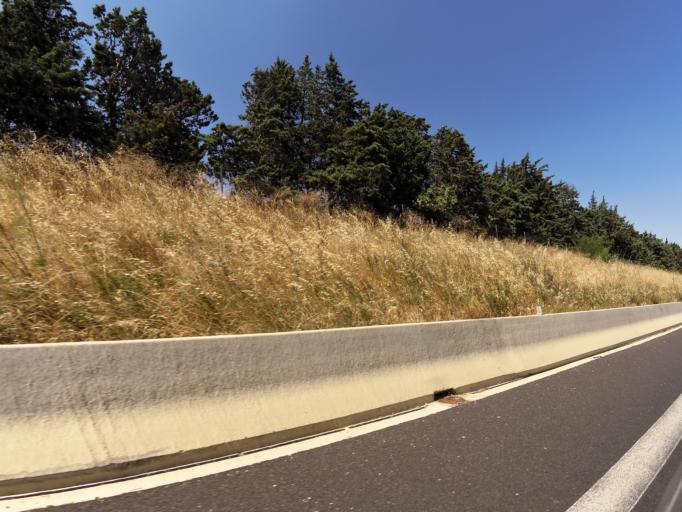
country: FR
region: Languedoc-Roussillon
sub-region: Departement de l'Herault
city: Le Cres
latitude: 43.6120
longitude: 3.9407
